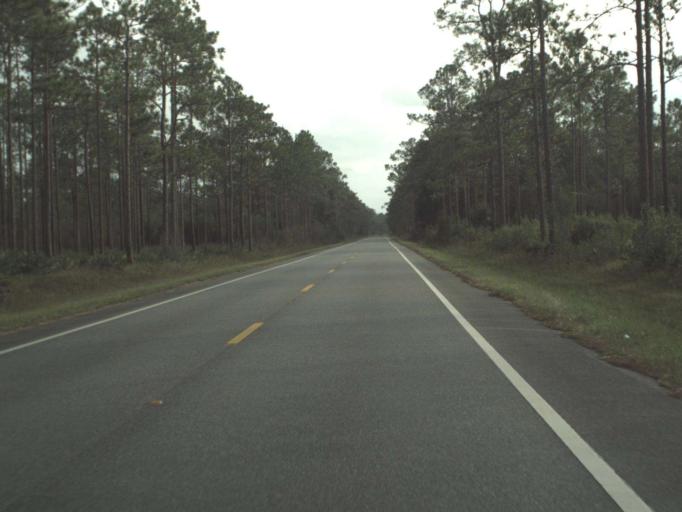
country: US
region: Florida
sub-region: Gulf County
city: Wewahitchka
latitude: 29.9844
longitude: -84.9759
